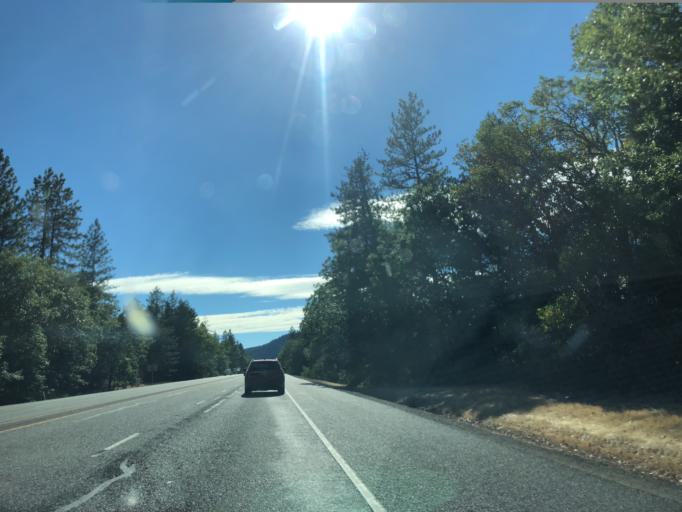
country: US
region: Oregon
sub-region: Josephine County
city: Redwood
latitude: 42.4122
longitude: -123.4154
